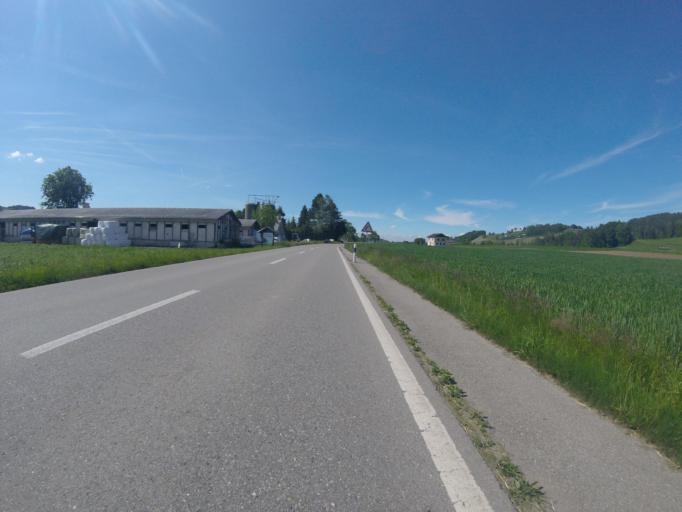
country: CH
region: Saint Gallen
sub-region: Wahlkreis Toggenburg
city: Ganterschwil
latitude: 47.3849
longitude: 9.0860
